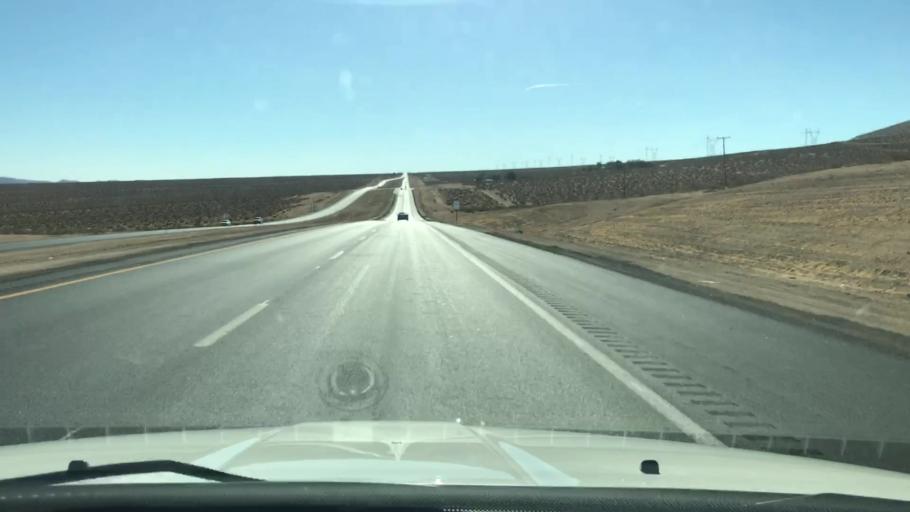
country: US
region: California
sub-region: Kern County
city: Inyokern
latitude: 35.6212
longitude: -117.8864
